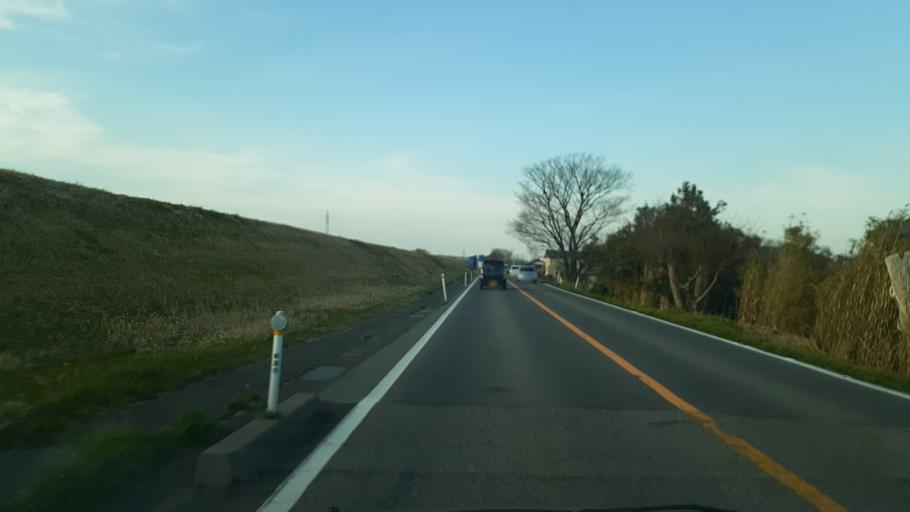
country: JP
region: Niigata
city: Niigata-shi
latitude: 37.8625
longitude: 139.0253
